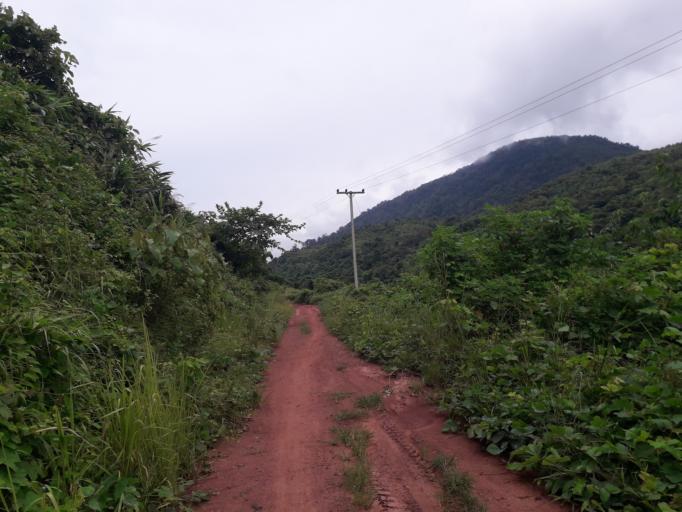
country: CN
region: Yunnan
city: Menglie
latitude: 22.2246
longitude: 101.6414
